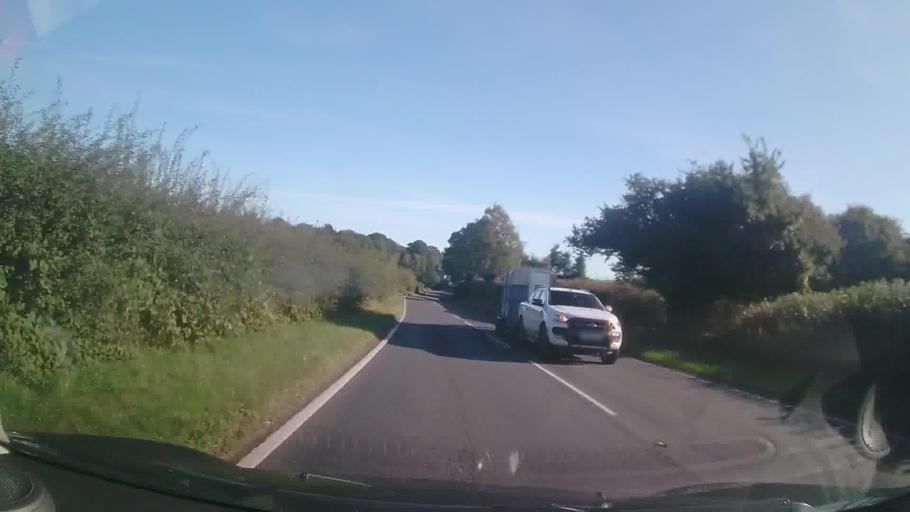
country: GB
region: Wales
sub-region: Sir Powys
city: Hay
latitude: 52.0139
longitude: -3.2357
